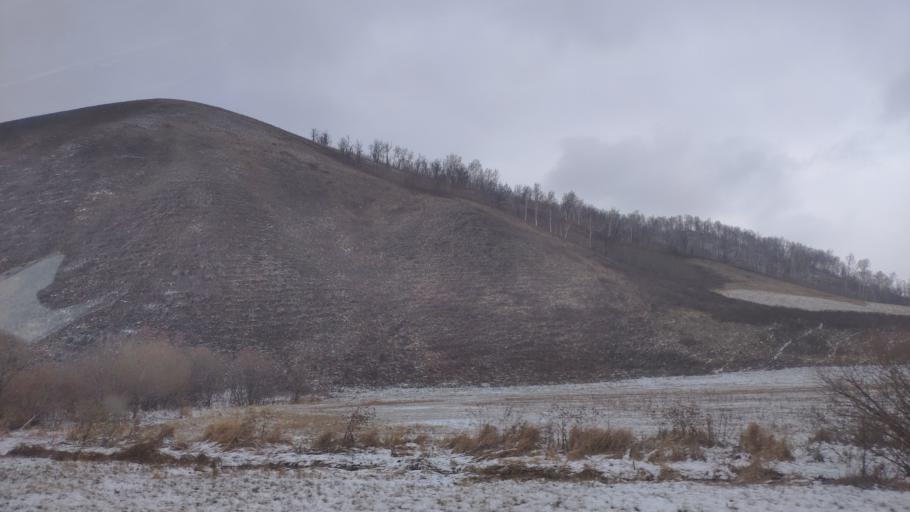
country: RU
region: Bashkortostan
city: Isyangulovo
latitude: 52.1609
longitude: 56.9201
